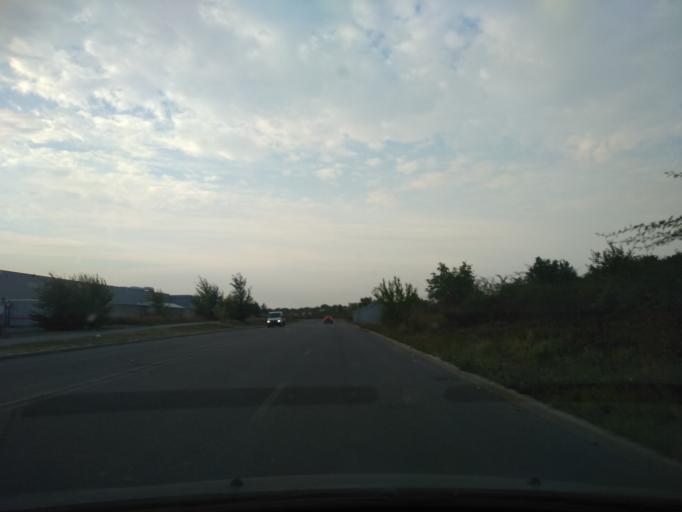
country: RO
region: Ilfov
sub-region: Comuna Otopeni
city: Otopeni
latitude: 44.5096
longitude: 26.0908
